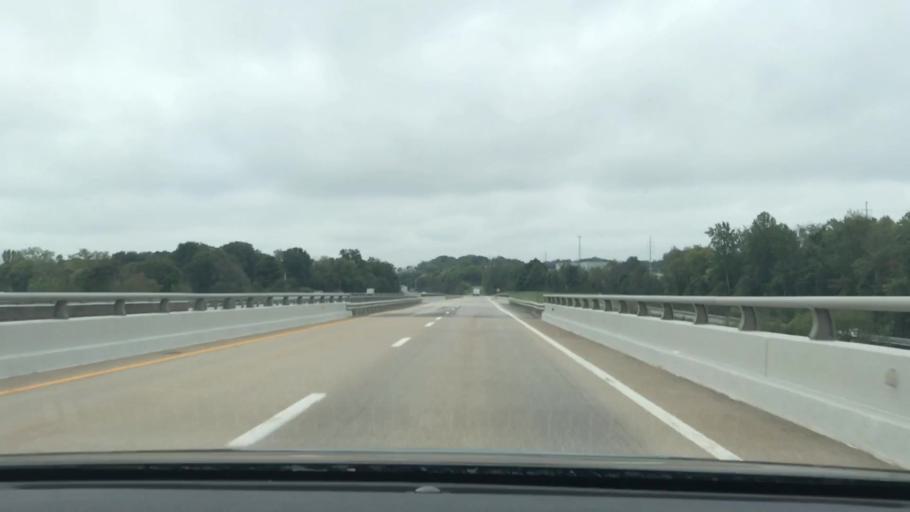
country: US
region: Kentucky
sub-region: Barren County
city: Glasgow
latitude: 36.9780
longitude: -85.9349
